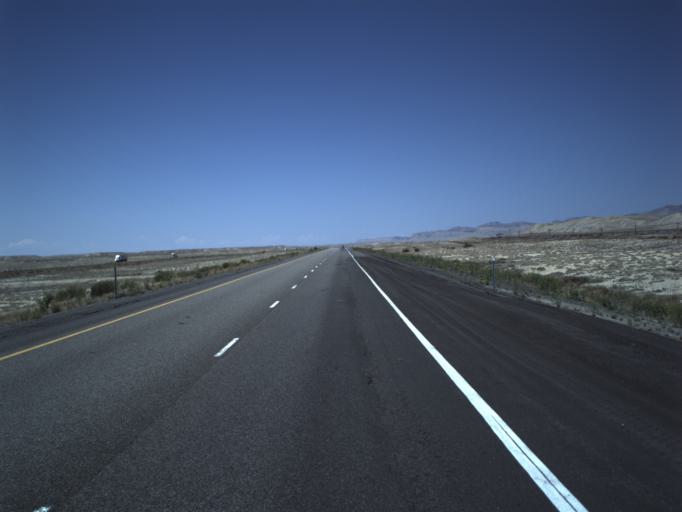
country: US
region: Utah
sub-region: Grand County
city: Moab
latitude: 38.9342
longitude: -109.4456
